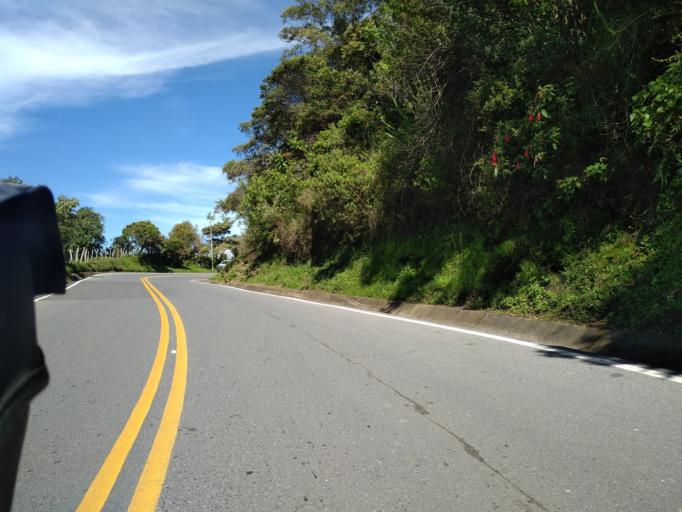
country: CO
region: Santander
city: Velez
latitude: 5.9989
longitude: -73.6848
